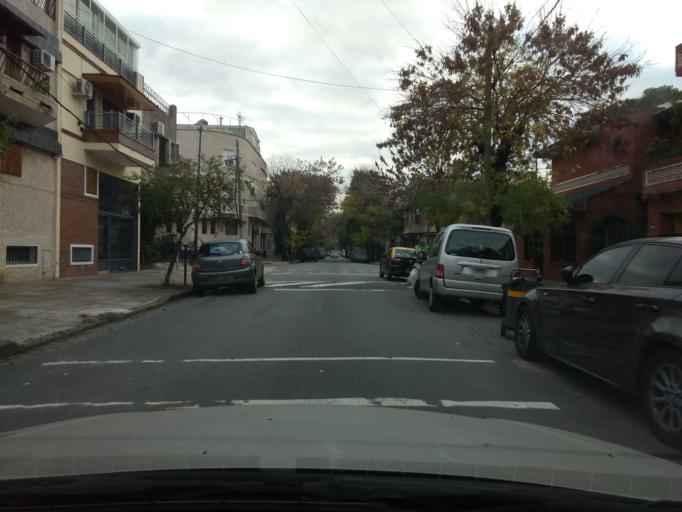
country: AR
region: Buenos Aires F.D.
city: Villa Santa Rita
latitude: -34.6104
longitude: -58.5122
